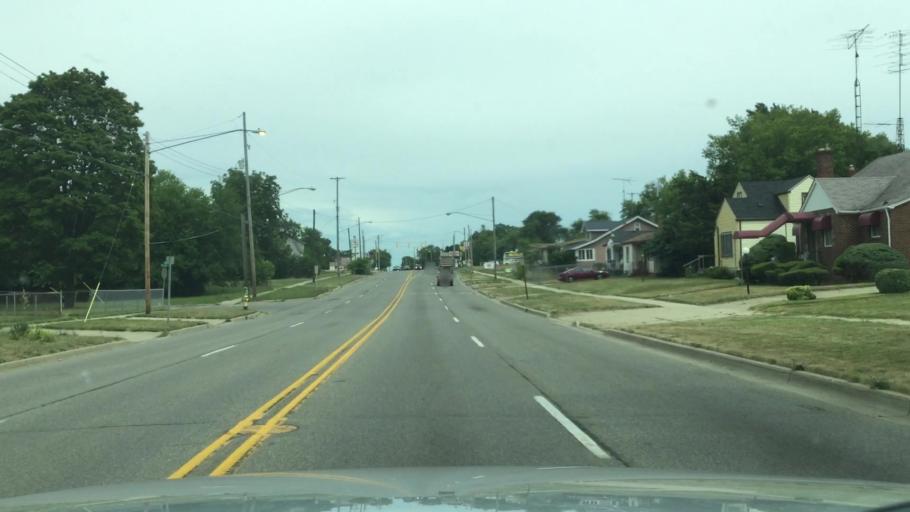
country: US
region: Michigan
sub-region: Genesee County
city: Beecher
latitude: 43.0610
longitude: -83.6972
